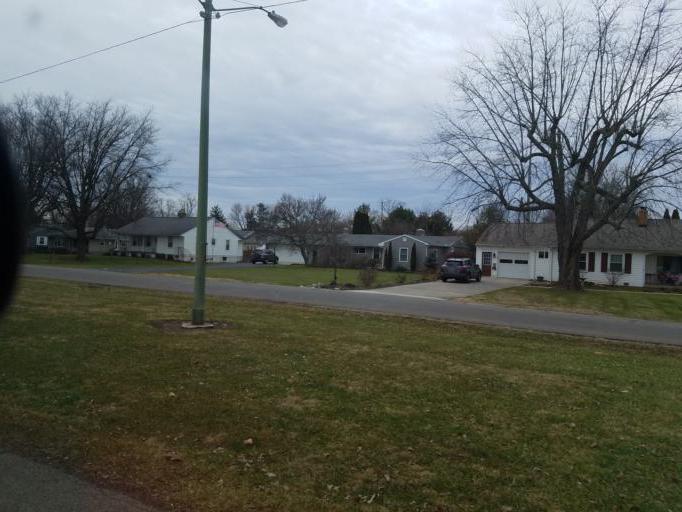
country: US
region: Ohio
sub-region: Marion County
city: Marion
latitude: 40.5832
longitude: -83.1064
